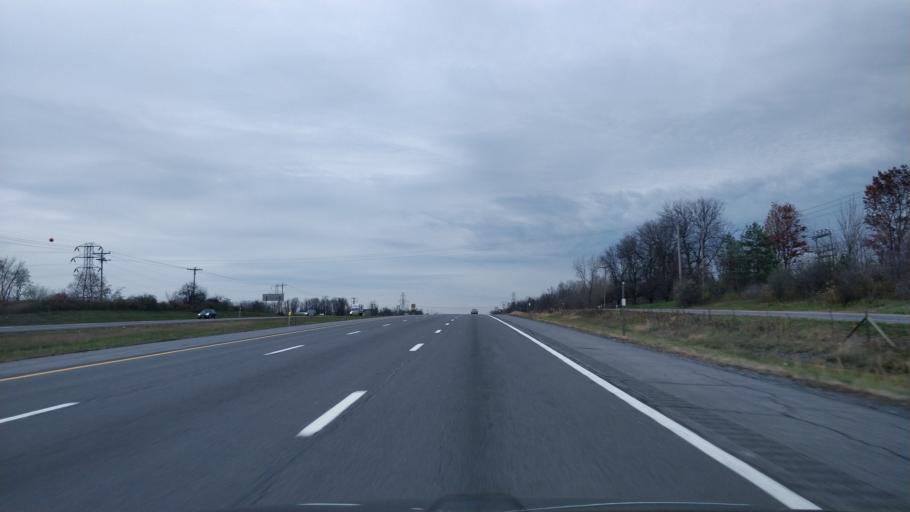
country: US
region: New York
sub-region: Onondaga County
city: North Syracuse
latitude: 43.1809
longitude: -76.1176
